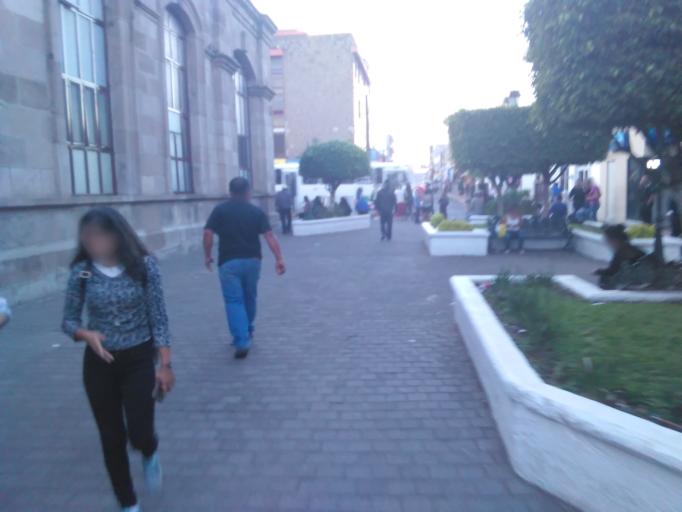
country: MX
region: Nayarit
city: Tepic
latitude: 21.5127
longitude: -104.8928
